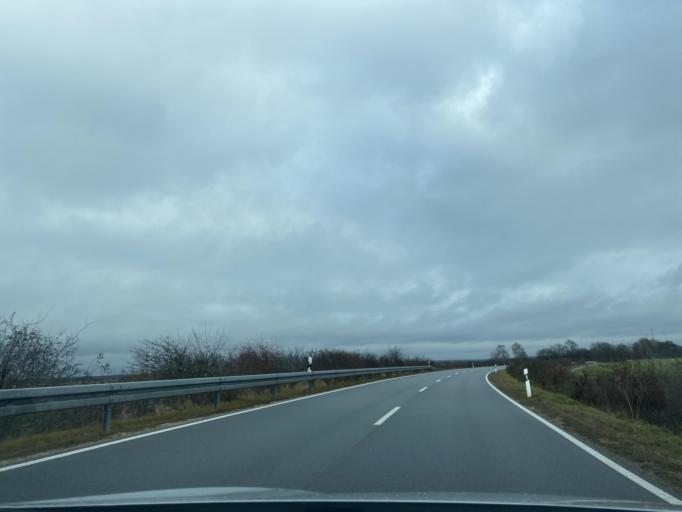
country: PL
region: Lower Silesian Voivodeship
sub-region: Powiat zgorzelecki
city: Piensk
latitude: 51.2387
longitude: 14.9853
